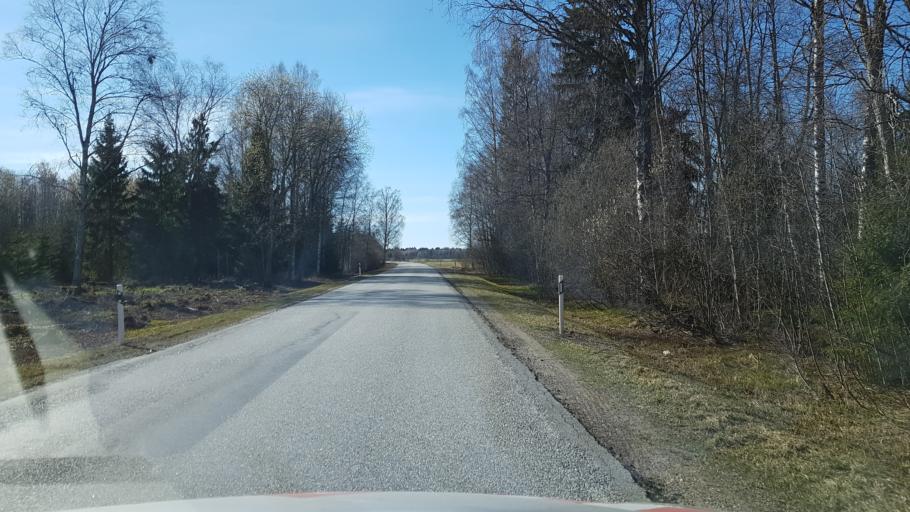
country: EE
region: Ida-Virumaa
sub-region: Aseri vald
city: Aseri
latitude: 59.2327
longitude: 26.7546
